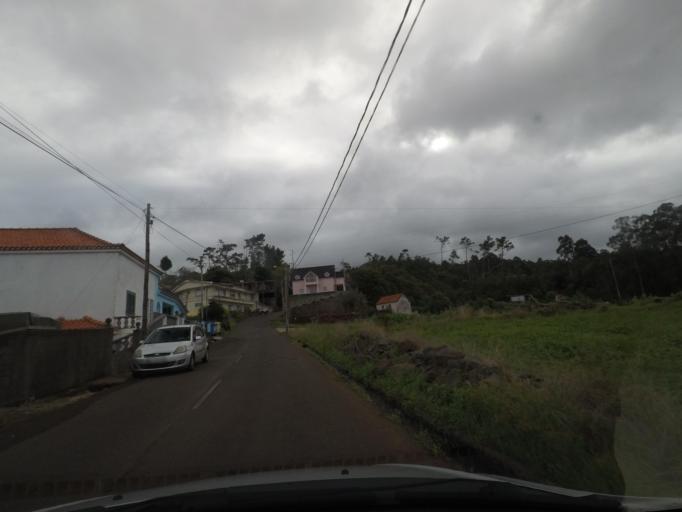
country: PT
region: Madeira
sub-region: Santana
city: Santana
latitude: 32.7876
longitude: -16.8749
